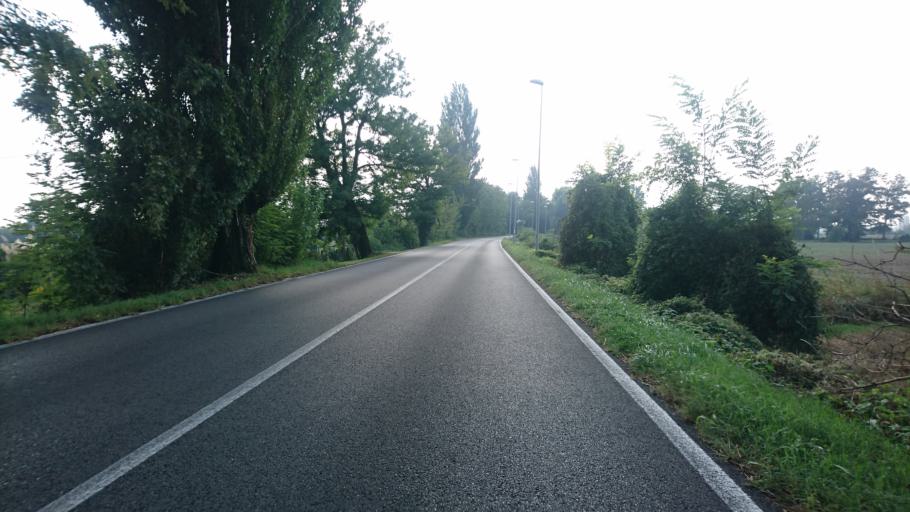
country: IT
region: Veneto
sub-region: Provincia di Rovigo
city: Grignano Polesine
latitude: 45.0453
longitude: 11.7748
